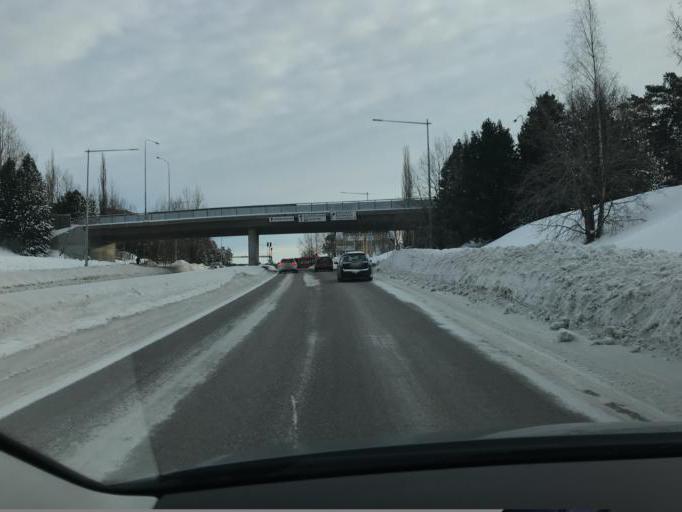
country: SE
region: Norrbotten
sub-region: Lulea Kommun
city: Lulea
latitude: 65.5933
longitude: 22.1595
